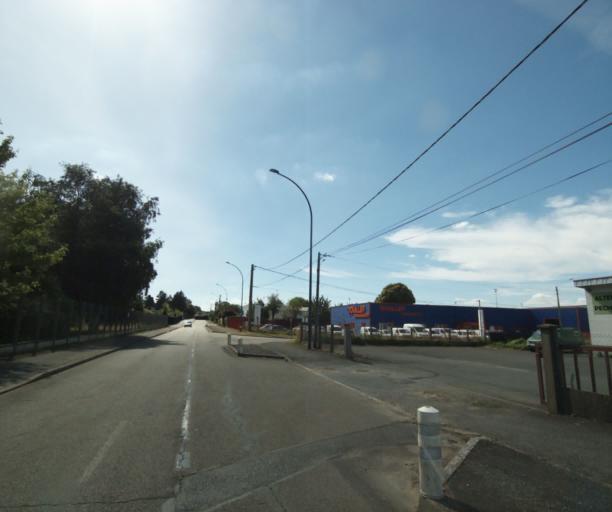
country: FR
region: Pays de la Loire
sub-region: Departement de la Mayenne
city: Change
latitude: 48.0708
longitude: -0.7975
